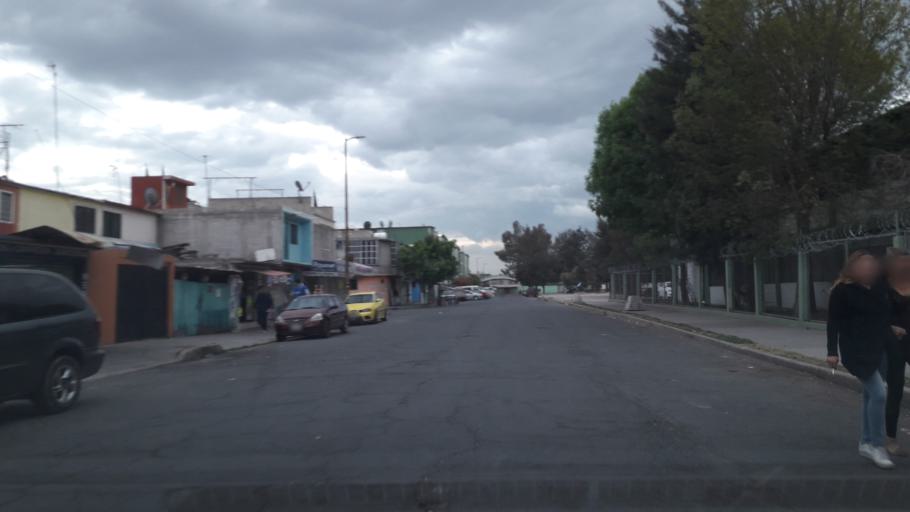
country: MX
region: Mexico
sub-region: Jaltenco
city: Alborada Jaltenco
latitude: 19.6626
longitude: -99.0706
